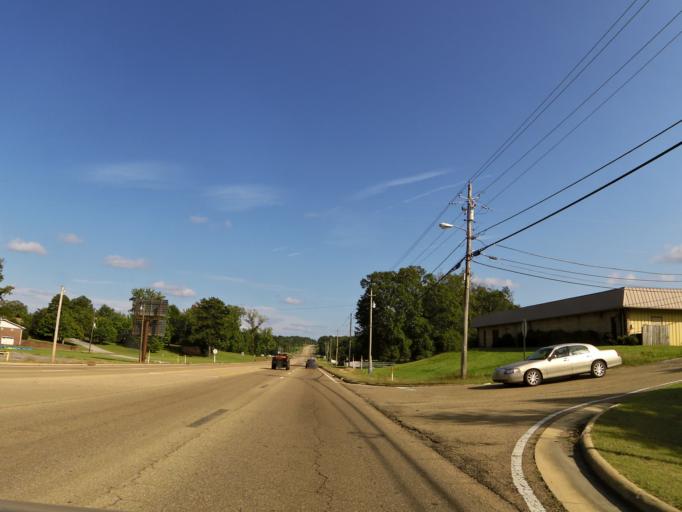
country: US
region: Mississippi
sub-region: Alcorn County
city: Farmington
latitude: 34.9043
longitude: -88.4836
